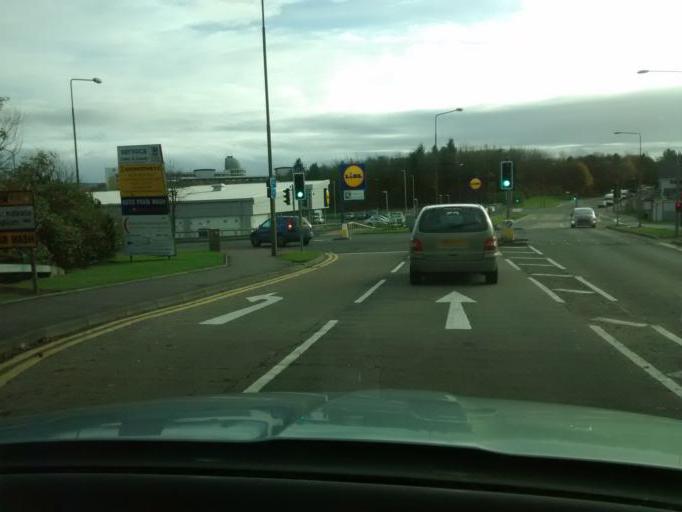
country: GB
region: Scotland
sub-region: West Lothian
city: Livingston
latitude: 55.8871
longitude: -3.5261
